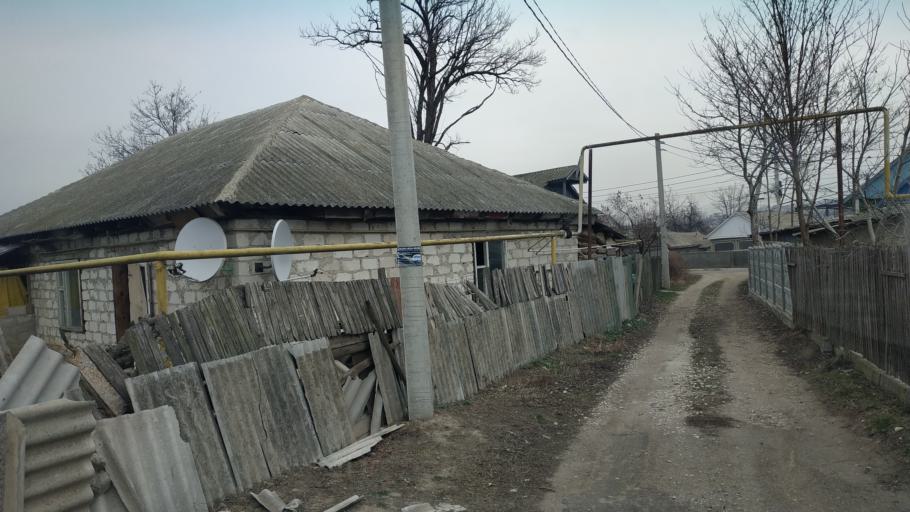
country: MD
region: Chisinau
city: Singera
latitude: 46.9121
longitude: 28.9763
